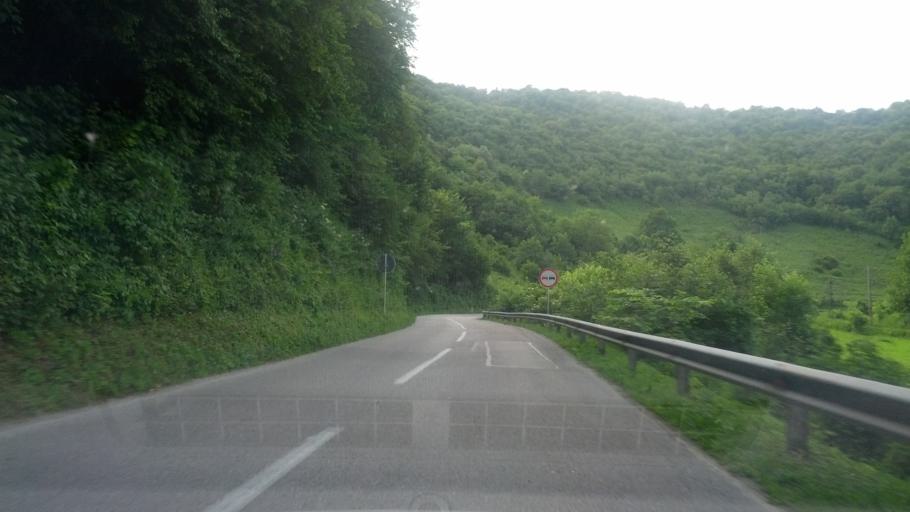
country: BA
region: Federation of Bosnia and Herzegovina
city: Stijena
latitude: 44.9028
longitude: 15.9931
